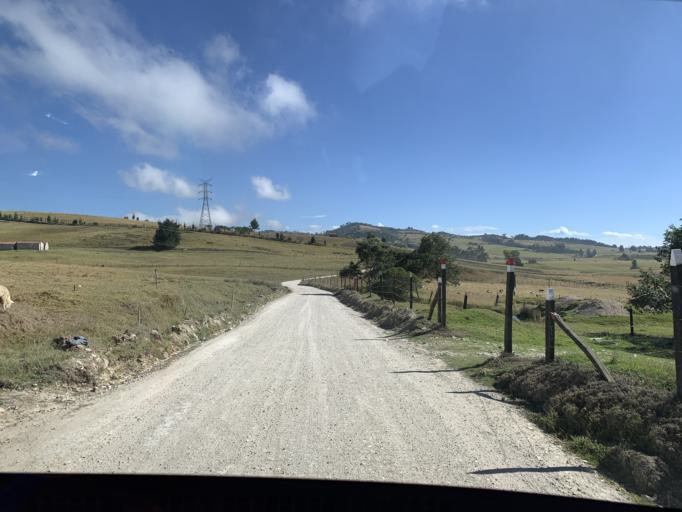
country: CO
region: Boyaca
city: Tuta
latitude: 5.6725
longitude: -73.1484
